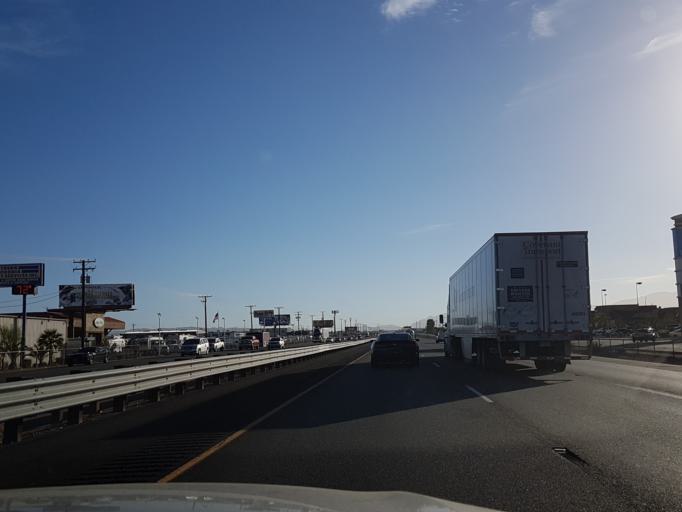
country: US
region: California
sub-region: San Bernardino County
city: Mountain View Acres
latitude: 34.4655
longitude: -117.3502
